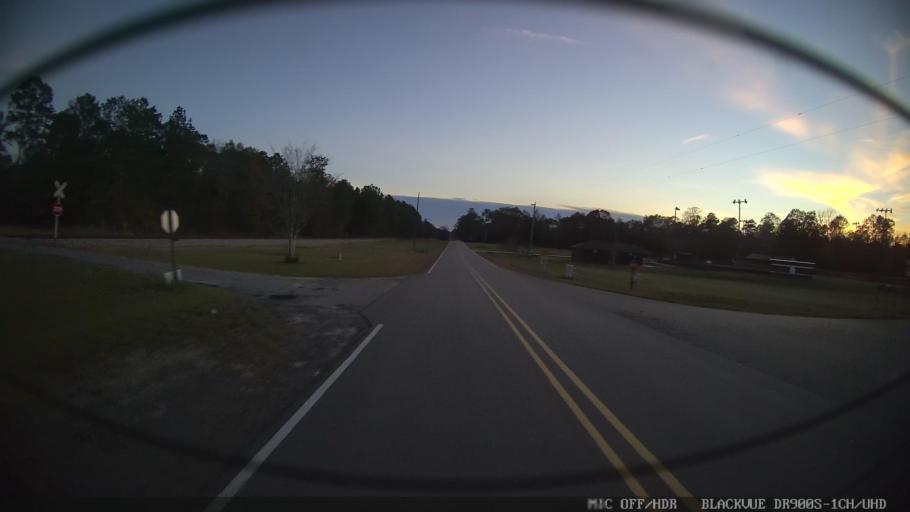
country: US
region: Mississippi
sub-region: Perry County
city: New Augusta
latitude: 31.0679
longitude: -89.1856
